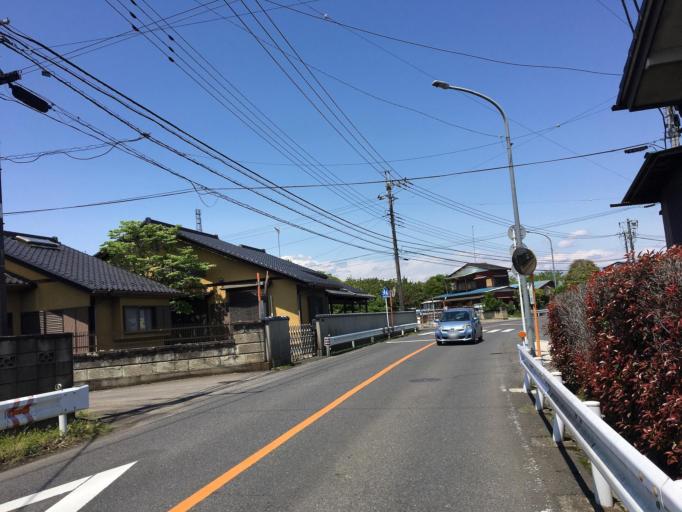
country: JP
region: Tochigi
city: Tochigi
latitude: 36.3653
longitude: 139.7231
